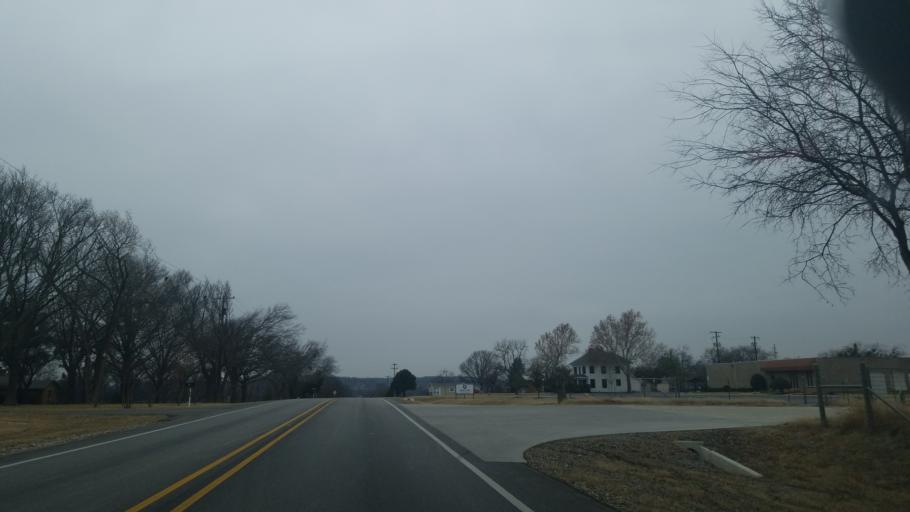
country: US
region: Texas
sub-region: Denton County
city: Denton
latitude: 33.1595
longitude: -97.1419
